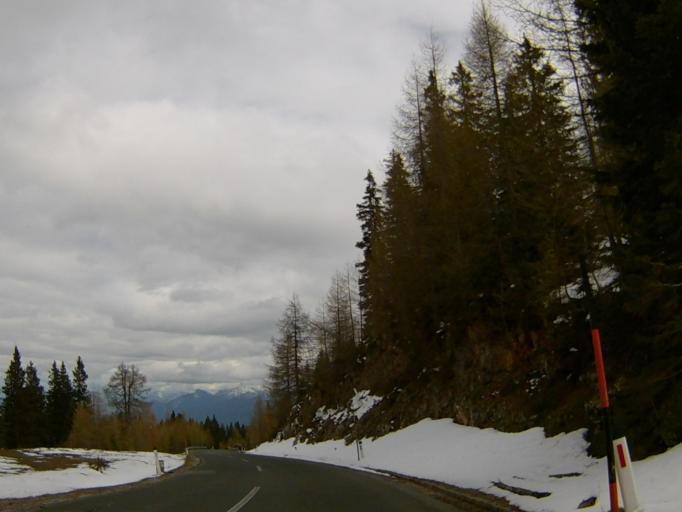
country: AT
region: Carinthia
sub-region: Politischer Bezirk Villach Land
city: Arnoldstein
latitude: 46.5956
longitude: 13.7159
